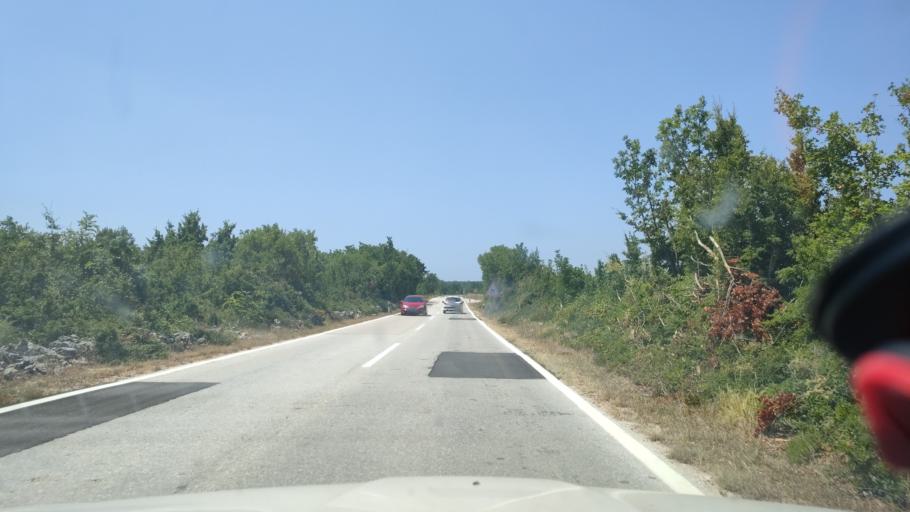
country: HR
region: Sibensko-Kniniska
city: Kistanje
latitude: 43.9721
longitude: 15.9102
